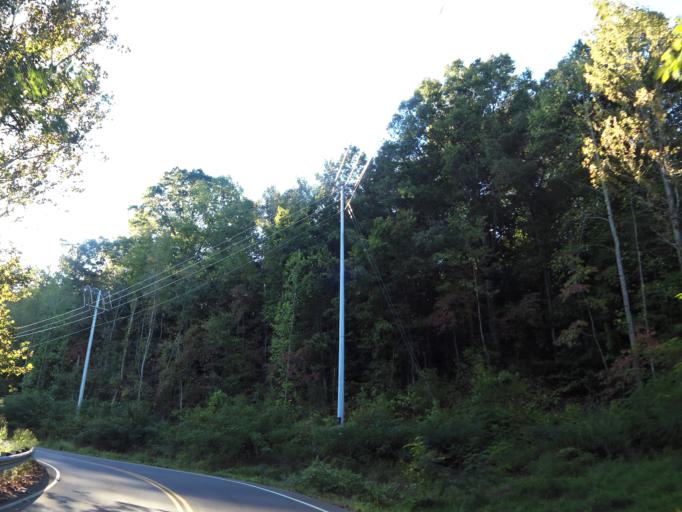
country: US
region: Tennessee
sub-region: Knox County
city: Knoxville
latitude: 35.9082
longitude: -83.9404
